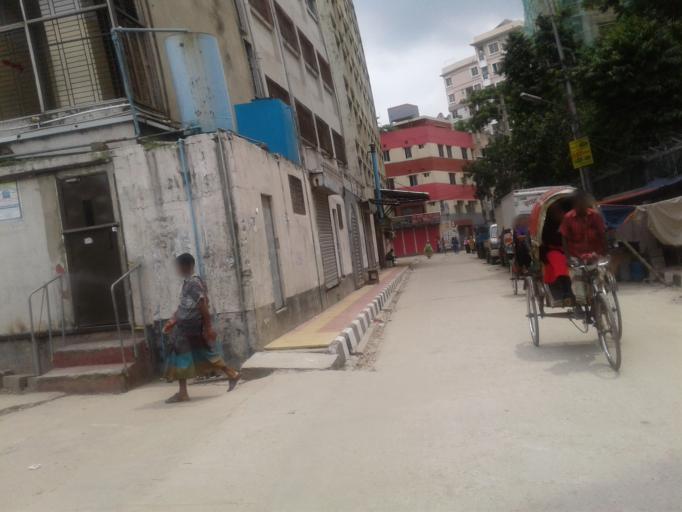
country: BD
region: Dhaka
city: Azimpur
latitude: 23.8037
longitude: 90.3769
